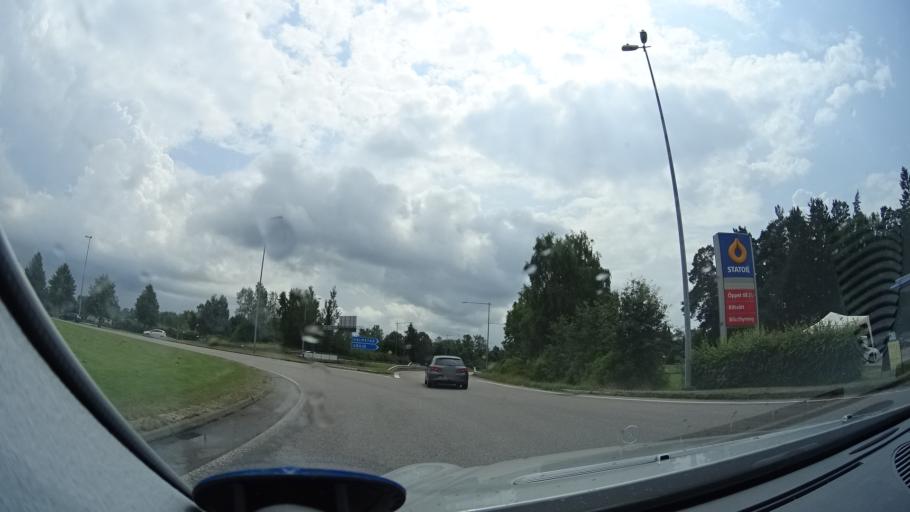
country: SE
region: Kalmar
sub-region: Nybro Kommun
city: Nybro
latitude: 56.7349
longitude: 15.9321
